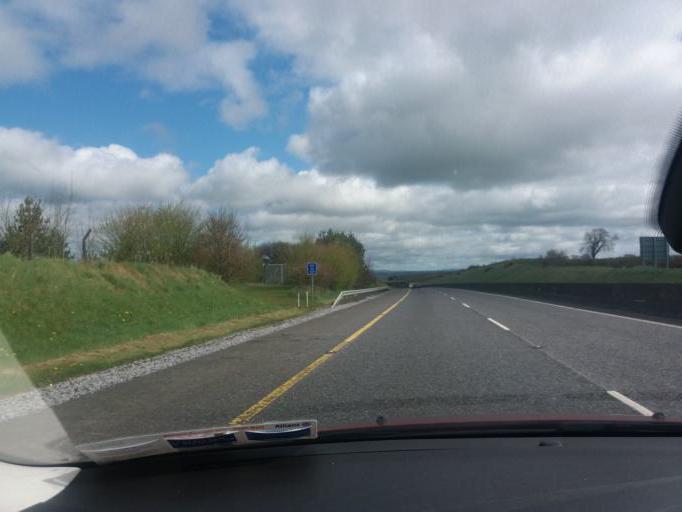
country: IE
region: Munster
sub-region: County Cork
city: Watergrasshill
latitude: 52.0336
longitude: -8.3202
